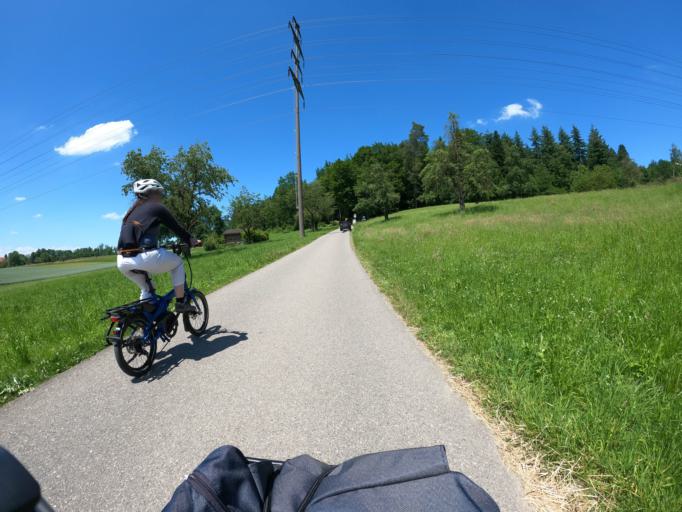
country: CH
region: Zug
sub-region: Zug
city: Steinhausen
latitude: 47.2033
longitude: 8.4944
